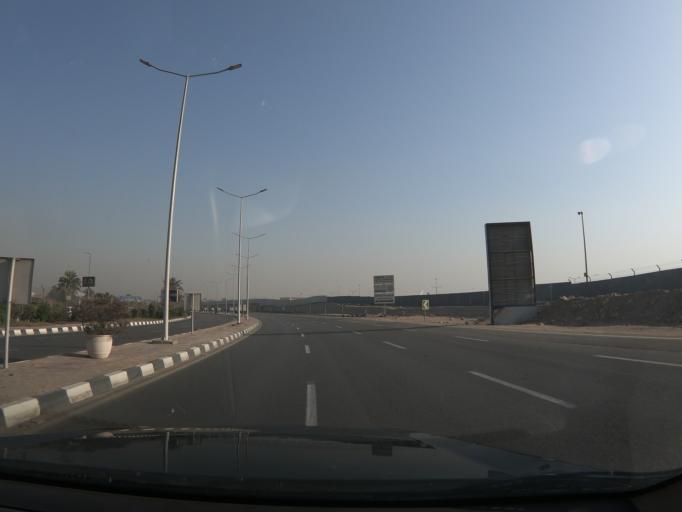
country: EG
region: Muhafazat al Qalyubiyah
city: Al Khankah
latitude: 30.1029
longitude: 31.3879
